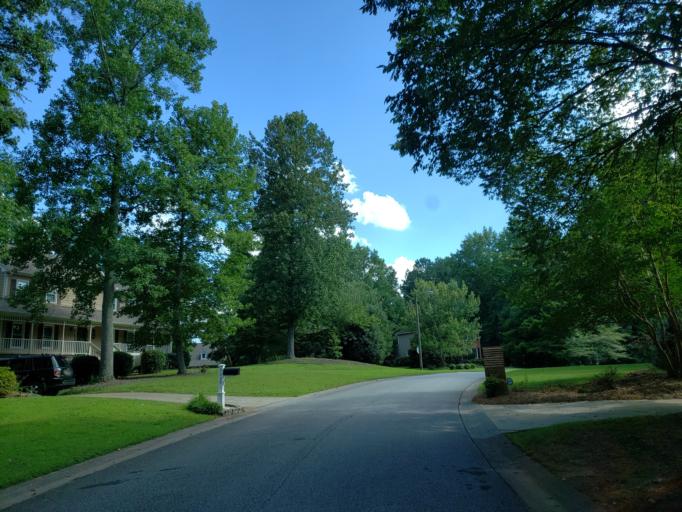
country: US
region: Georgia
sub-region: Cherokee County
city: Holly Springs
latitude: 34.1761
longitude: -84.4241
